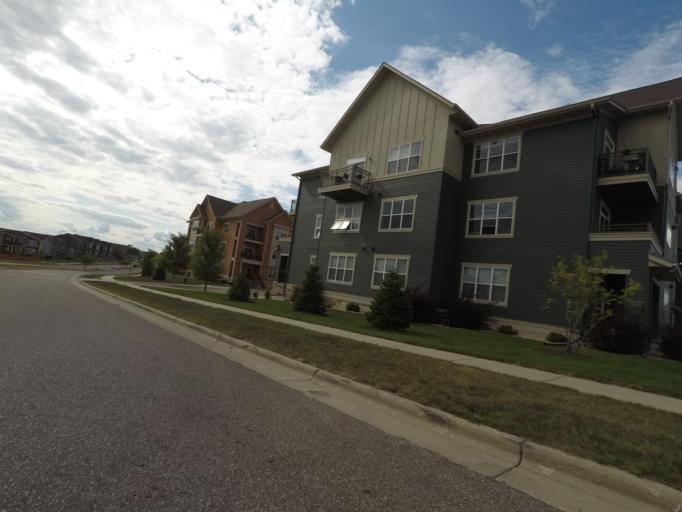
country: US
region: Wisconsin
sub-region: Dane County
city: Middleton
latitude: 43.0569
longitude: -89.5473
